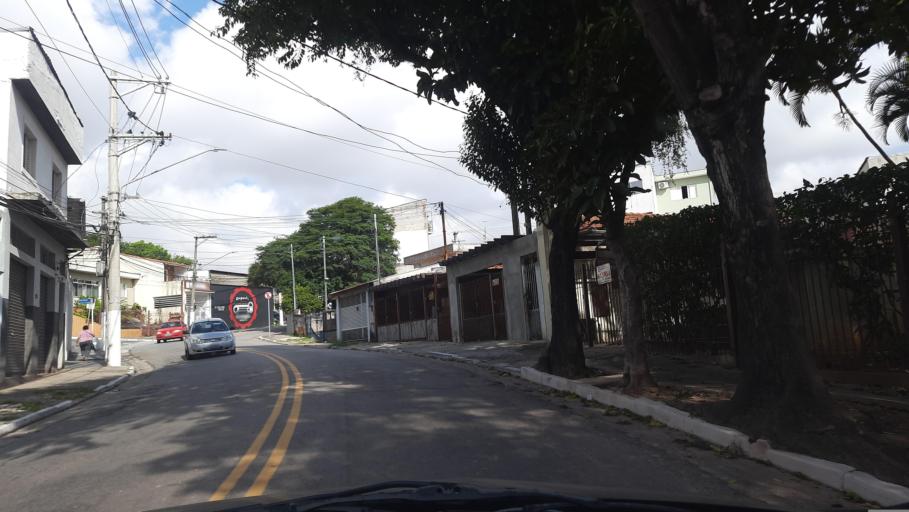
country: BR
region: Sao Paulo
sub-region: Sao Paulo
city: Sao Paulo
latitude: -23.4957
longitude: -46.6906
